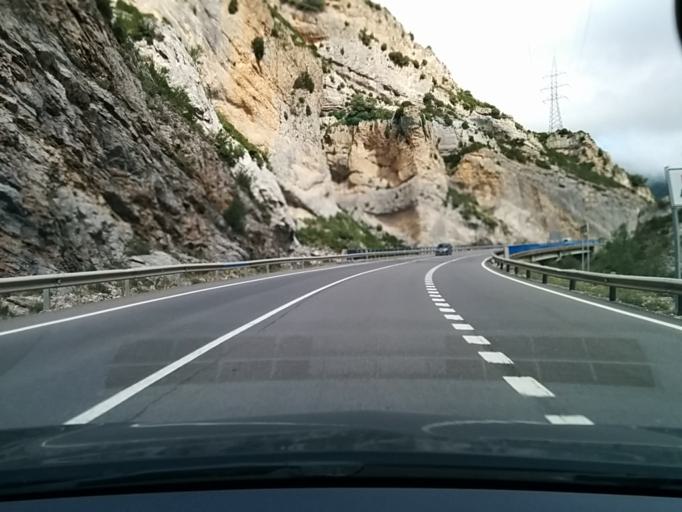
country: ES
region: Aragon
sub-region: Provincia de Huesca
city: Arguis
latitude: 42.3009
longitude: -0.4287
